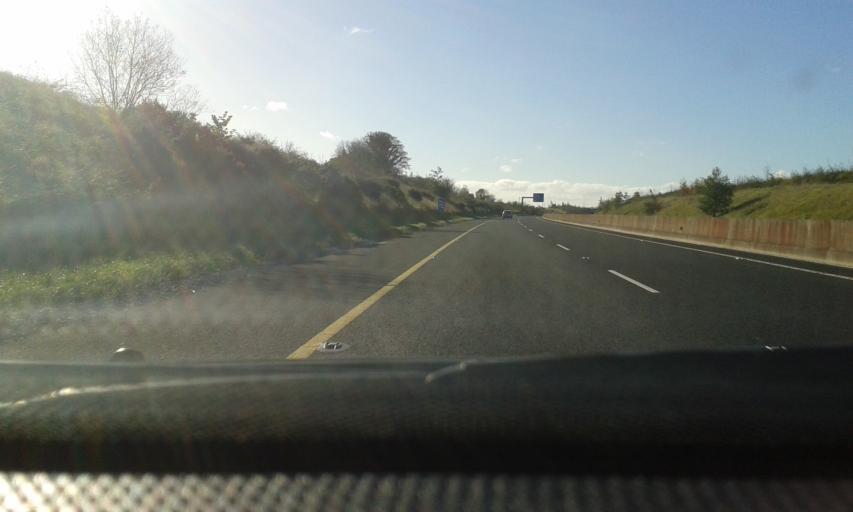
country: IE
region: Munster
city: Thurles
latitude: 52.6293
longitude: -7.7666
